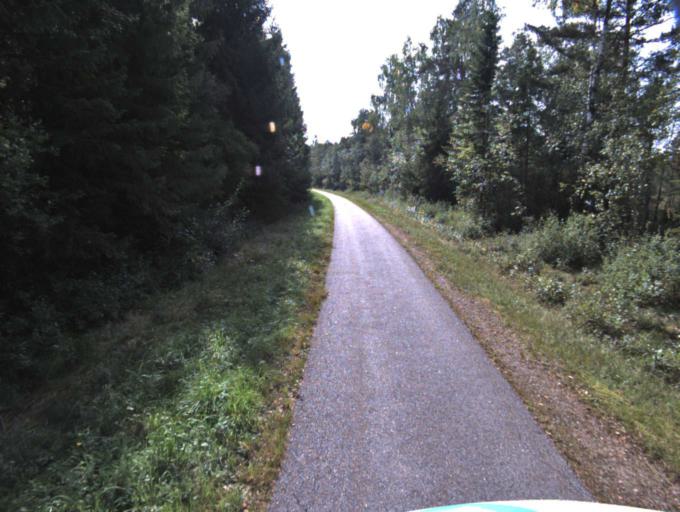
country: SE
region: Vaestra Goetaland
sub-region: Tranemo Kommun
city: Limmared
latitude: 57.6151
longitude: 13.3435
